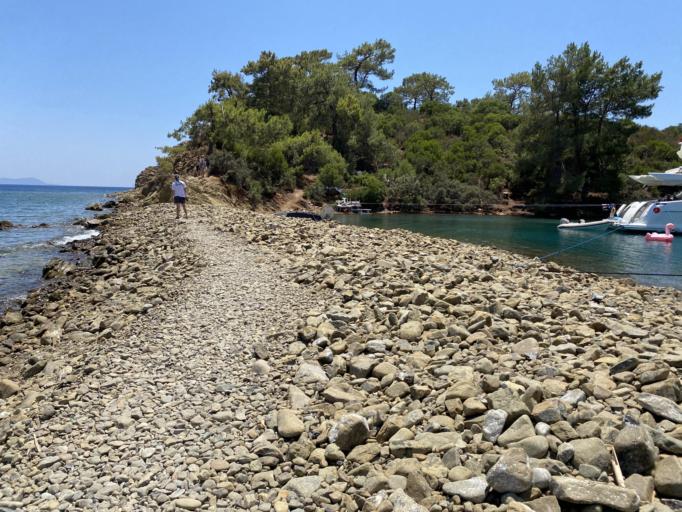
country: TR
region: Mugla
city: Goecek
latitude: 36.7083
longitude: 28.9348
